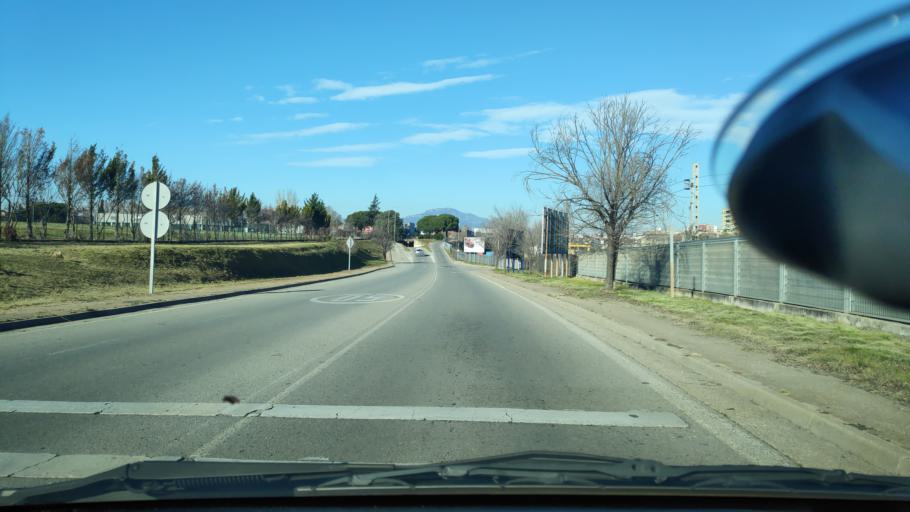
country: ES
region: Catalonia
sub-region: Provincia de Barcelona
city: Sabadell
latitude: 41.5255
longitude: 2.1064
